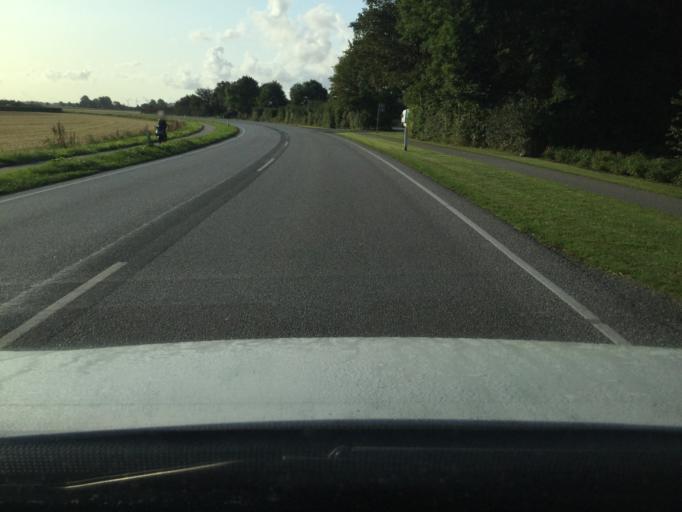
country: DK
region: Zealand
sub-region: Lolland Kommune
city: Nakskov
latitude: 54.8148
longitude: 11.1610
